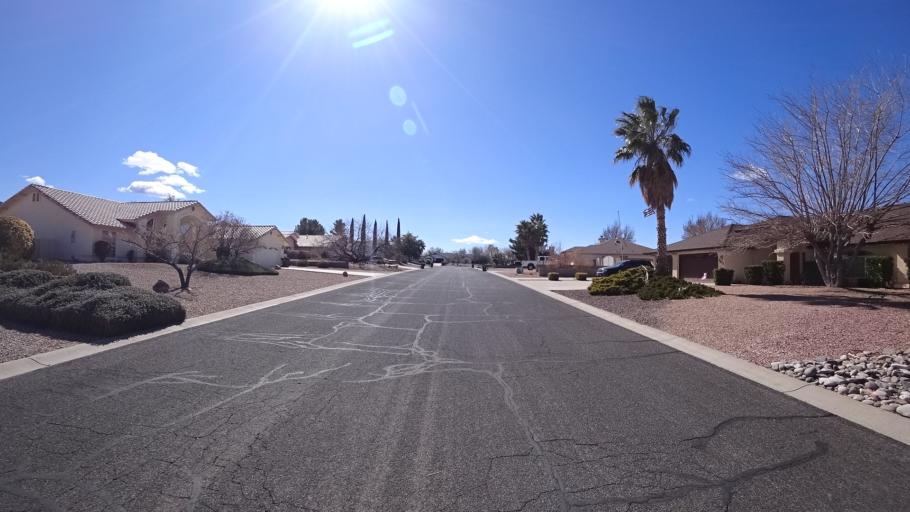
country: US
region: Arizona
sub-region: Mohave County
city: Kingman
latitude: 35.1992
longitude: -113.9696
